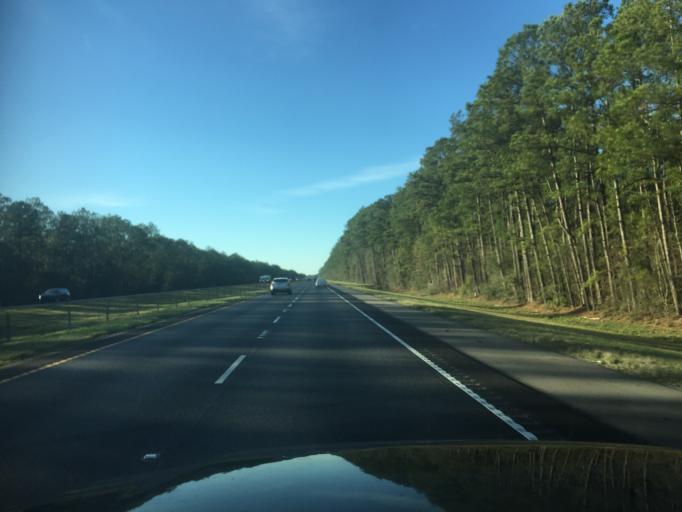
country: US
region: Louisiana
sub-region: Saint Tammany Parish
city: Lacombe
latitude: 30.3629
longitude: -89.9403
